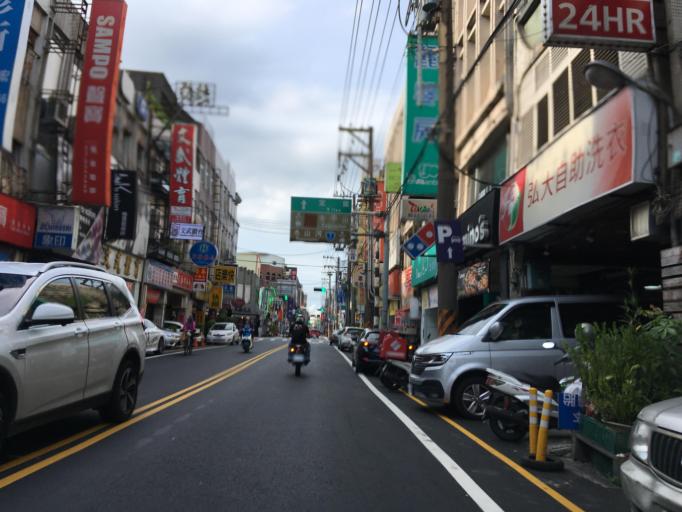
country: TW
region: Taiwan
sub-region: Yilan
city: Yilan
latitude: 24.6742
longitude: 121.7708
